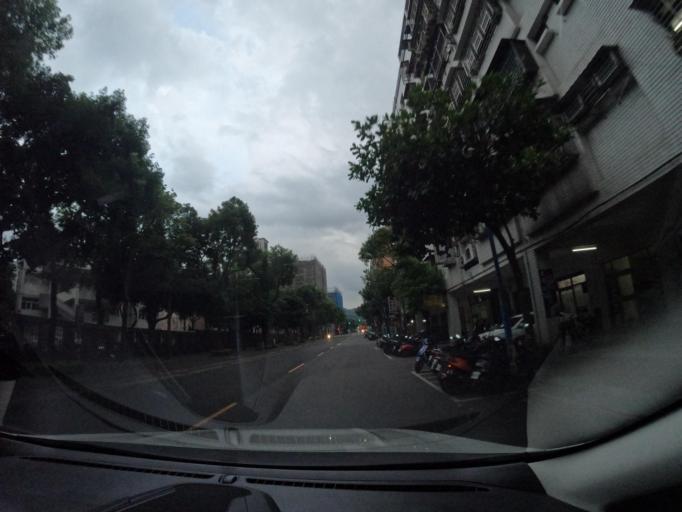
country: TW
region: Taipei
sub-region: Taipei
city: Banqiao
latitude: 24.9817
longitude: 121.4506
